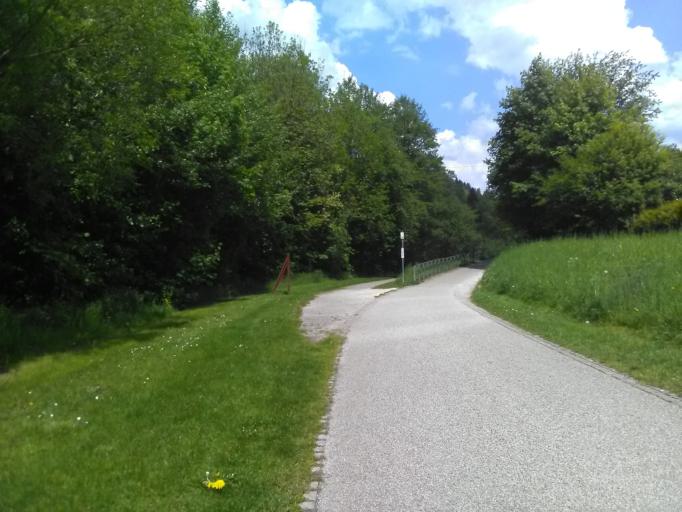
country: DE
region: Bavaria
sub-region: Upper Franconia
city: Kronach
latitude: 50.2317
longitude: 11.3161
